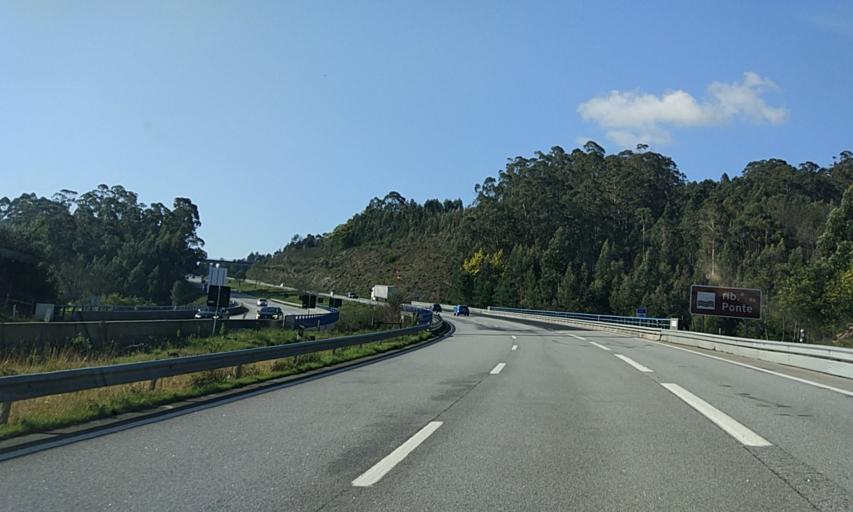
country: PT
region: Aveiro
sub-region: Sever do Vouga
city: Sever do Vouga
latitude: 40.6798
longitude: -8.2780
